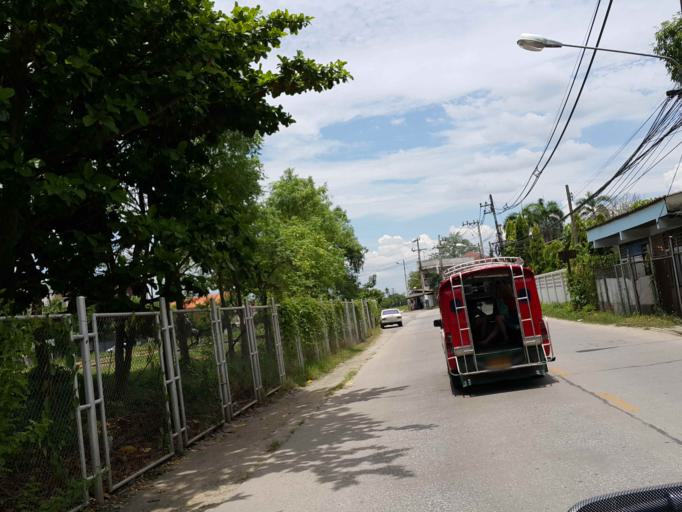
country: TH
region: Chiang Mai
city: Chiang Mai
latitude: 18.7755
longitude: 99.0170
